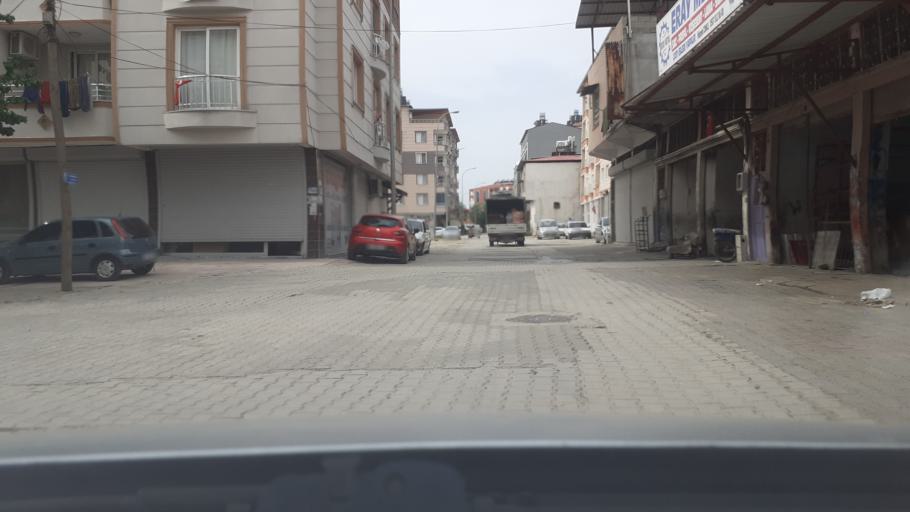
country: TR
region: Hatay
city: Kirikhan
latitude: 36.4962
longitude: 36.3622
